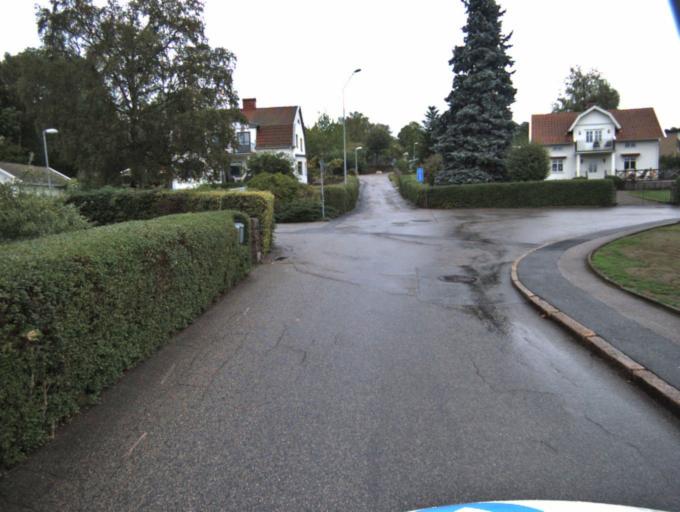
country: SE
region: Vaestra Goetaland
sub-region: Ulricehamns Kommun
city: Ulricehamn
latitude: 57.7926
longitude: 13.4221
